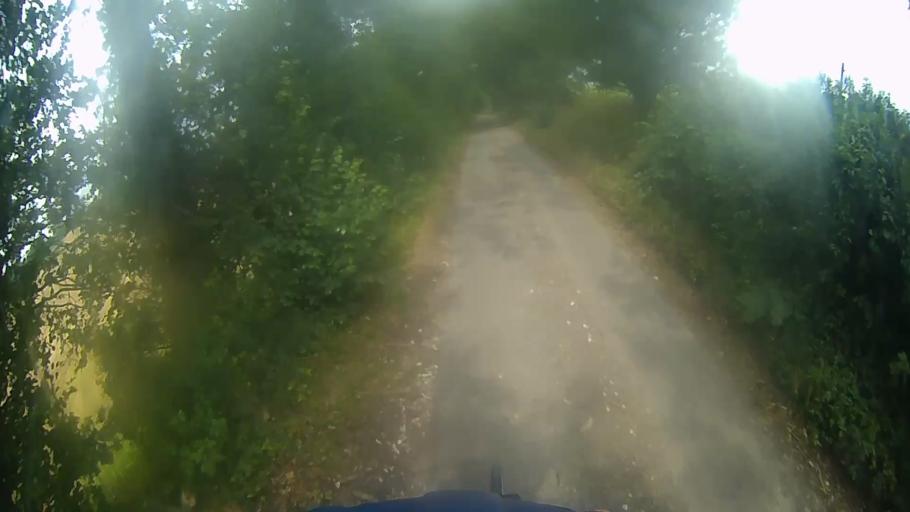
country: GB
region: England
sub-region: Hampshire
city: Overton
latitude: 51.2600
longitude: -1.3241
